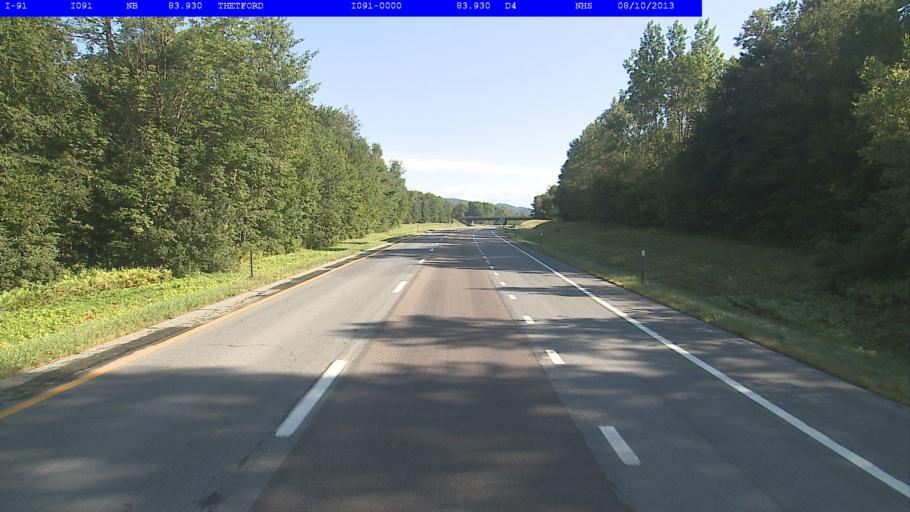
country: US
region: New Hampshire
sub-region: Grafton County
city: Lyme
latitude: 43.8085
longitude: -72.2179
